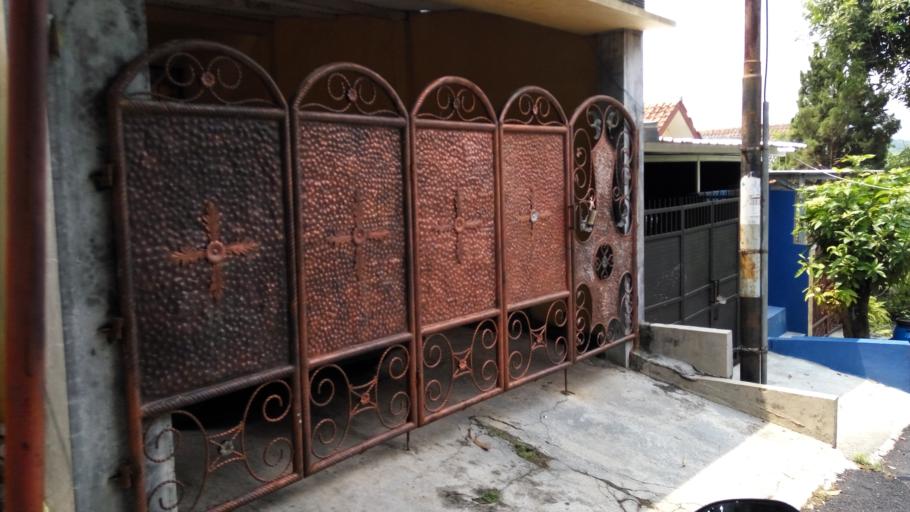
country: ID
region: Central Java
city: Mranggen
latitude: -7.0419
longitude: 110.4748
